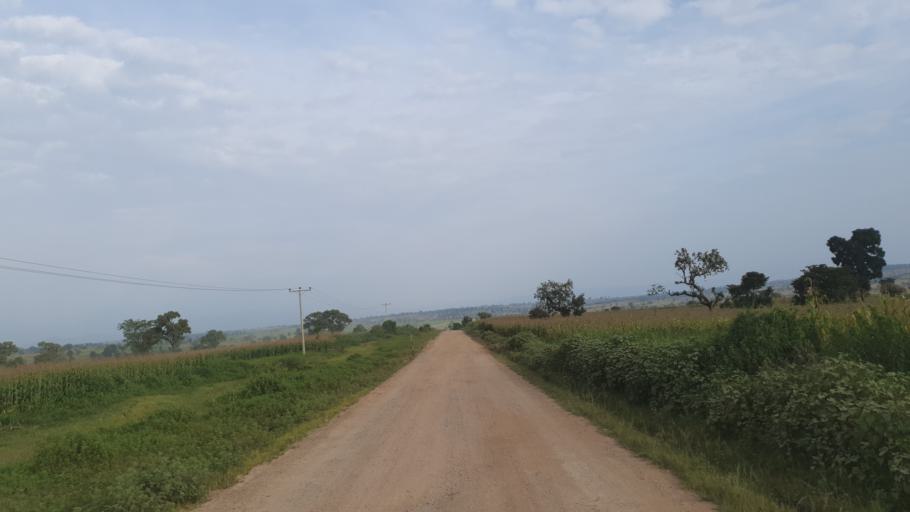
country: ET
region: Oromiya
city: Shambu
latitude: 9.5283
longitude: 36.5895
